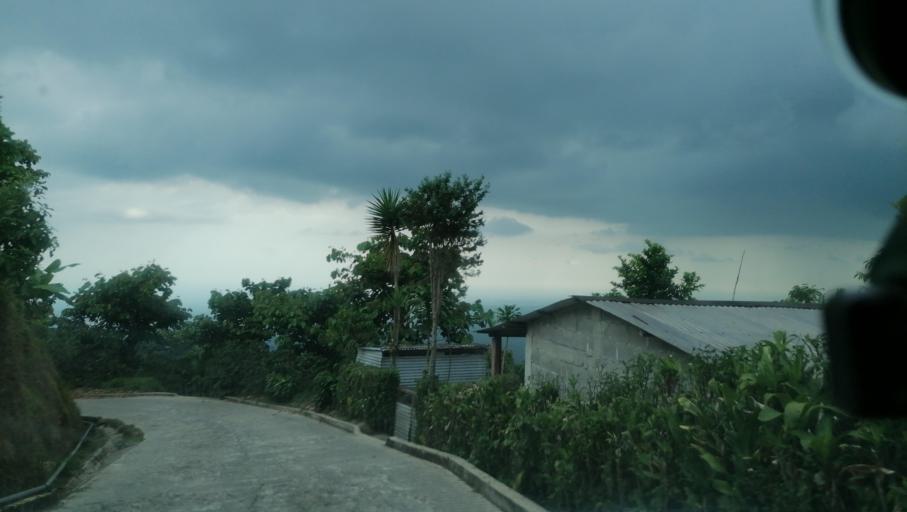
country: MX
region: Chiapas
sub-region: Cacahoatan
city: Benito Juarez
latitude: 15.0804
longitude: -92.1631
